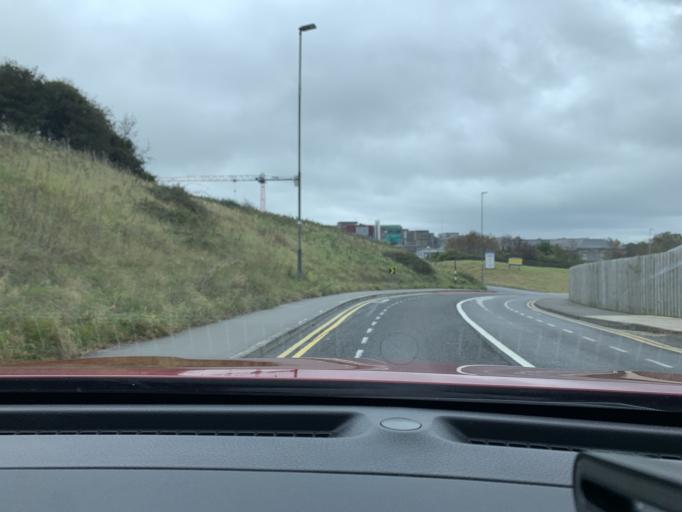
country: IE
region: Connaught
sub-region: Sligo
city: Sligo
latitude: 54.2738
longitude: -8.4678
